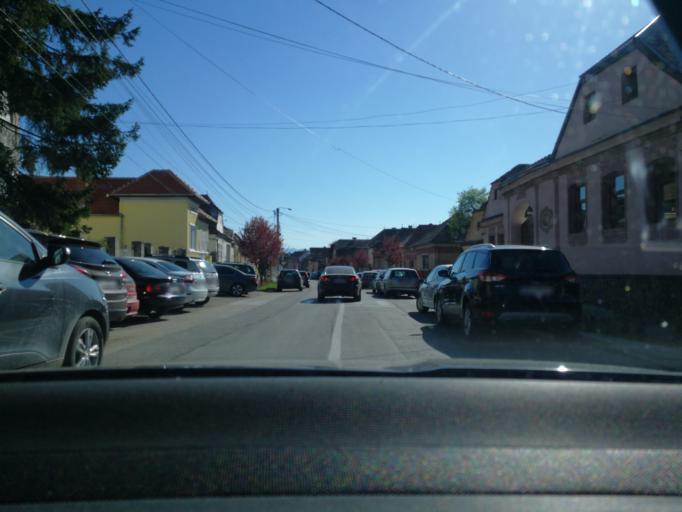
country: RO
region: Brasov
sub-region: Oras Rasnov
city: Rasnov
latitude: 45.5886
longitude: 25.4634
